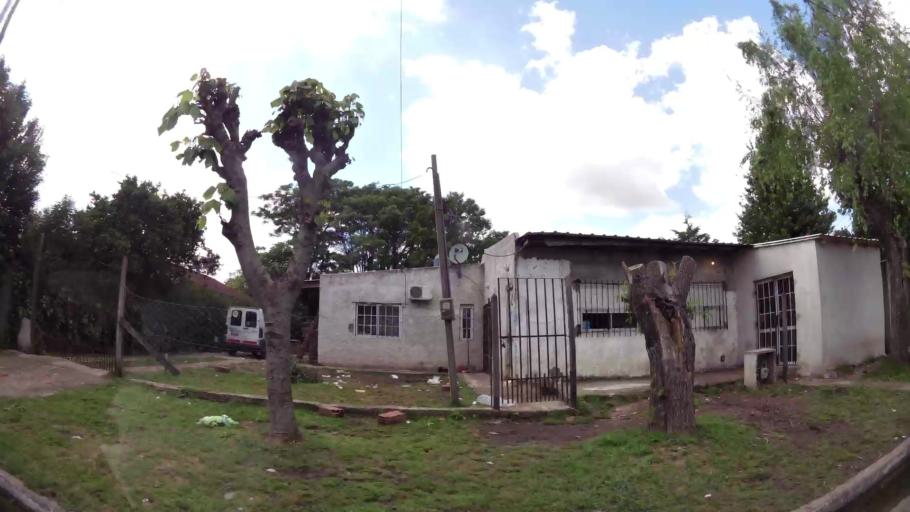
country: AR
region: Buenos Aires
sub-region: Partido de Quilmes
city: Quilmes
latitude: -34.8362
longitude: -58.1846
